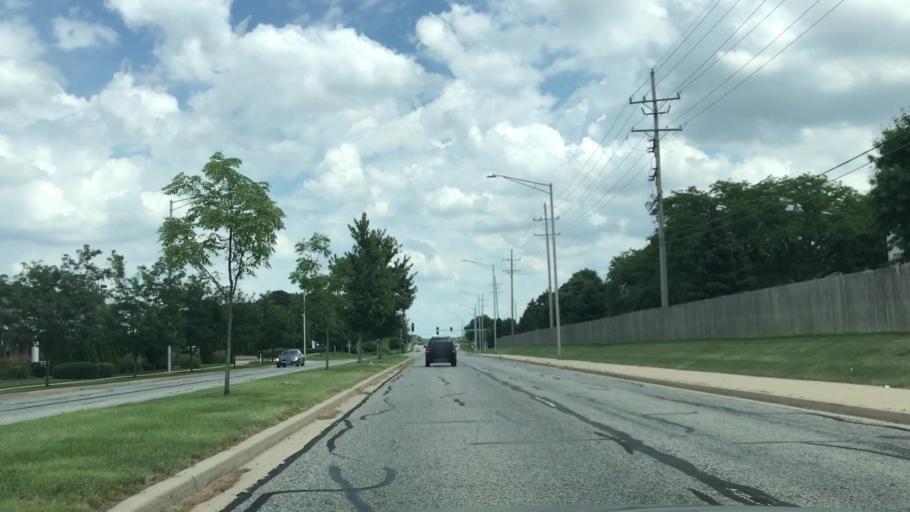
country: US
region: Illinois
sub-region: DuPage County
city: Warrenville
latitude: 41.7990
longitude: -88.2146
